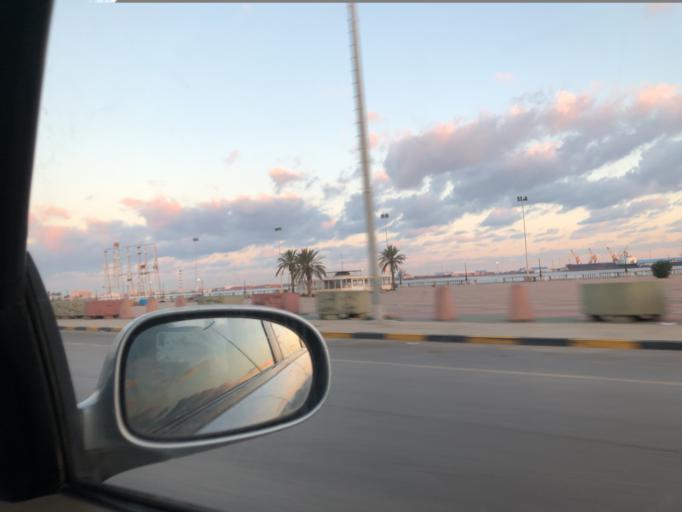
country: LY
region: Tripoli
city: Tripoli
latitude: 32.8946
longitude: 13.1889
